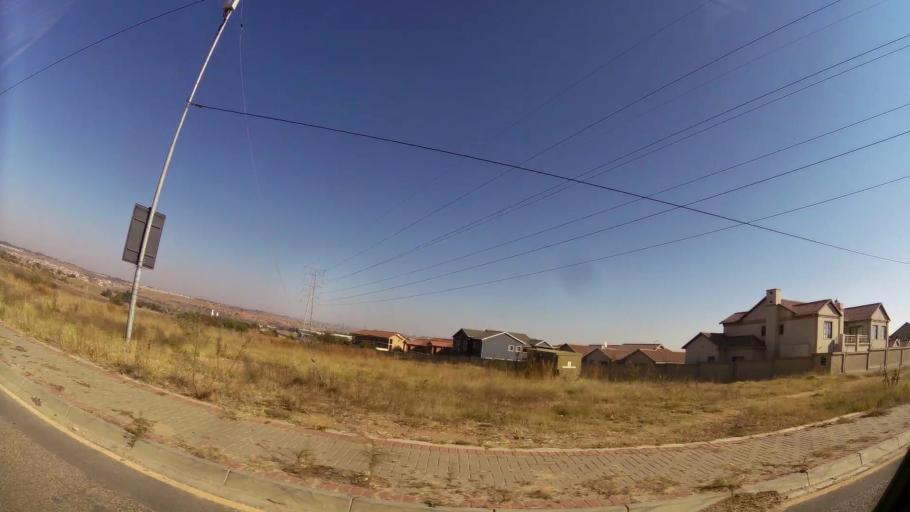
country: ZA
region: Gauteng
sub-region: City of Johannesburg Metropolitan Municipality
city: Midrand
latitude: -25.9202
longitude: 28.1326
